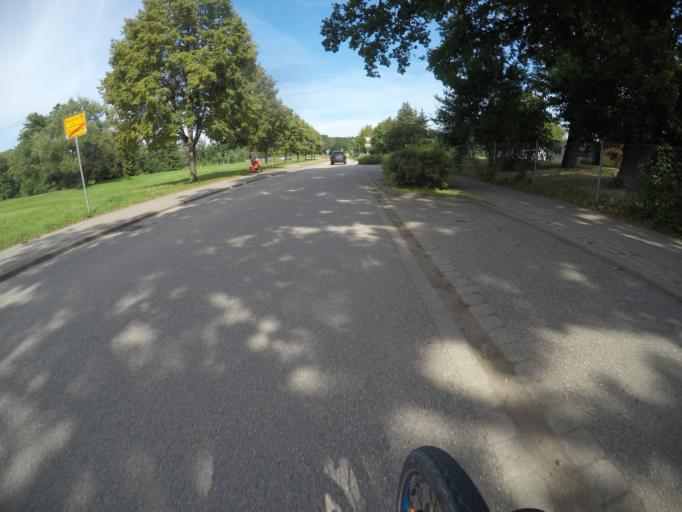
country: DE
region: Baden-Wuerttemberg
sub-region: Karlsruhe Region
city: Otisheim
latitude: 48.9669
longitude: 8.8019
